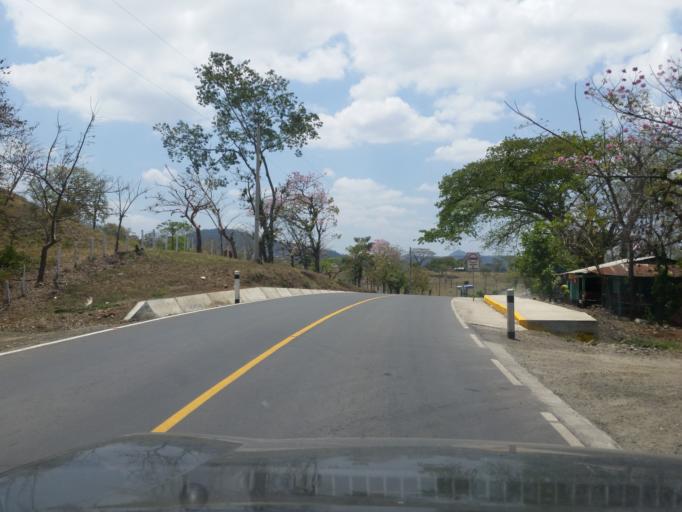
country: NI
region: Boaco
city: Boaco
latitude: 12.5123
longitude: -85.5793
